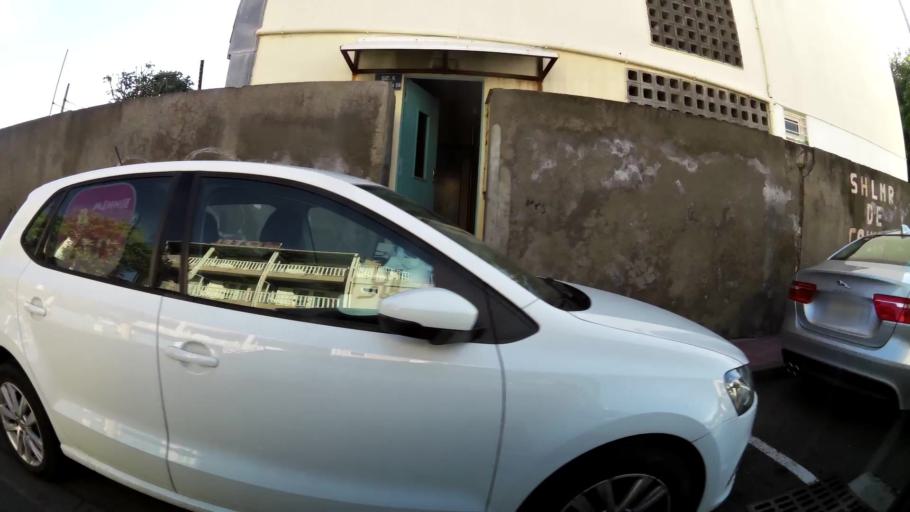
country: RE
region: Reunion
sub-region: Reunion
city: Saint-Pierre
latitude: -21.3427
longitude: 55.4696
